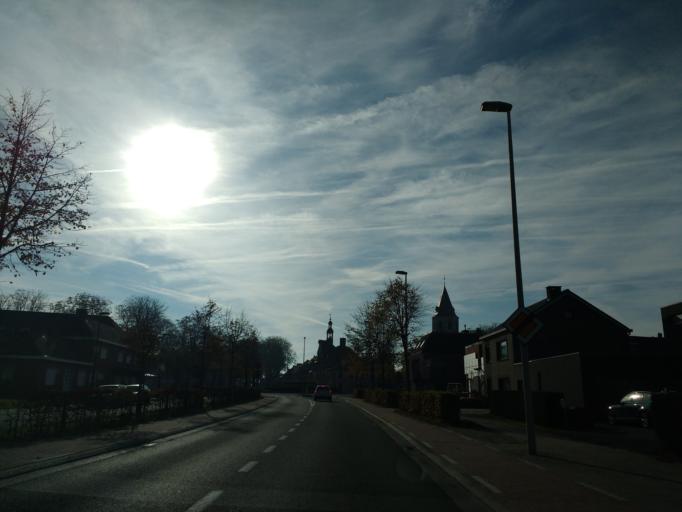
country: BE
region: Flanders
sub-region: Provincie Oost-Vlaanderen
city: Kaprijke
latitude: 51.2196
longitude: 3.6175
